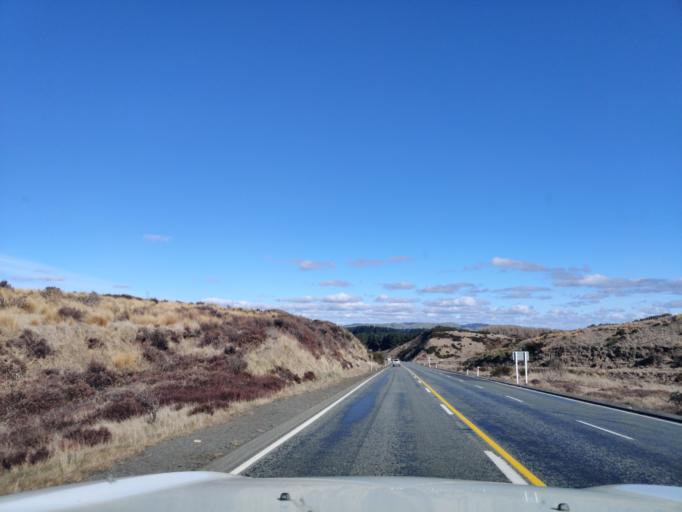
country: NZ
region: Manawatu-Wanganui
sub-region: Ruapehu District
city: Waiouru
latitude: -39.4350
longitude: 175.6839
